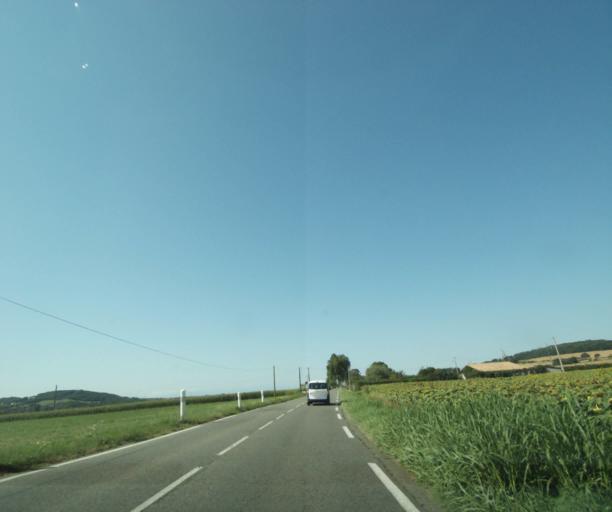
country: FR
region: Midi-Pyrenees
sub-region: Departement de la Haute-Garonne
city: Lagardelle-sur-Leze
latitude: 43.4052
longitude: 1.3701
